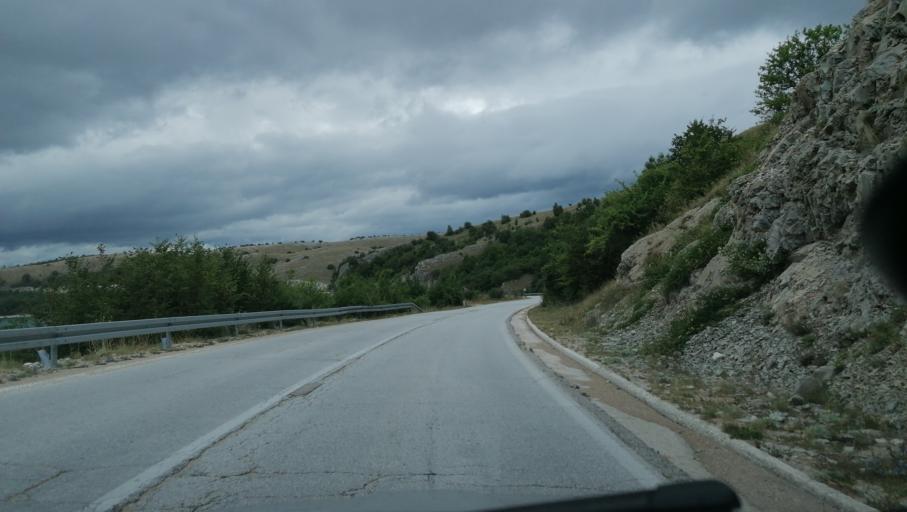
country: BA
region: Republika Srpska
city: Gacko
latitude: 43.1892
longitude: 18.5702
